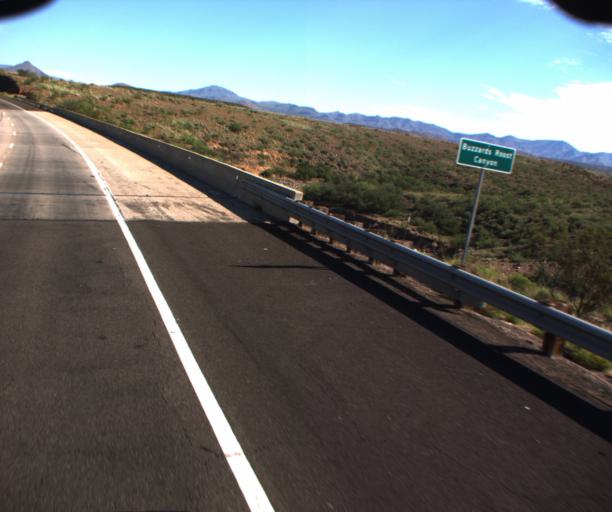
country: US
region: Arizona
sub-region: Greenlee County
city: Clifton
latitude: 32.9651
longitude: -109.2332
